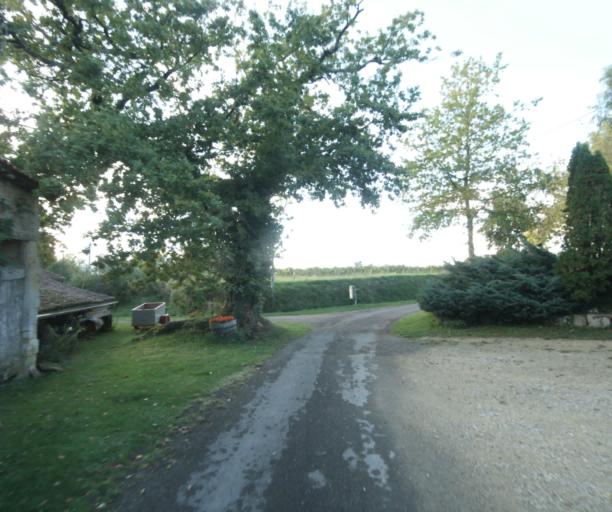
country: FR
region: Midi-Pyrenees
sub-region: Departement du Gers
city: Cazaubon
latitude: 43.8407
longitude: -0.0950
